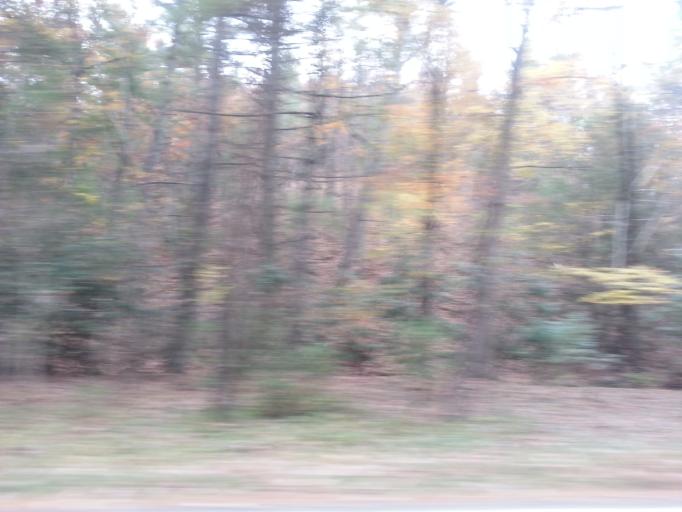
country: US
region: Virginia
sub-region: Bland County
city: Bland
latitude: 37.0467
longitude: -81.0662
